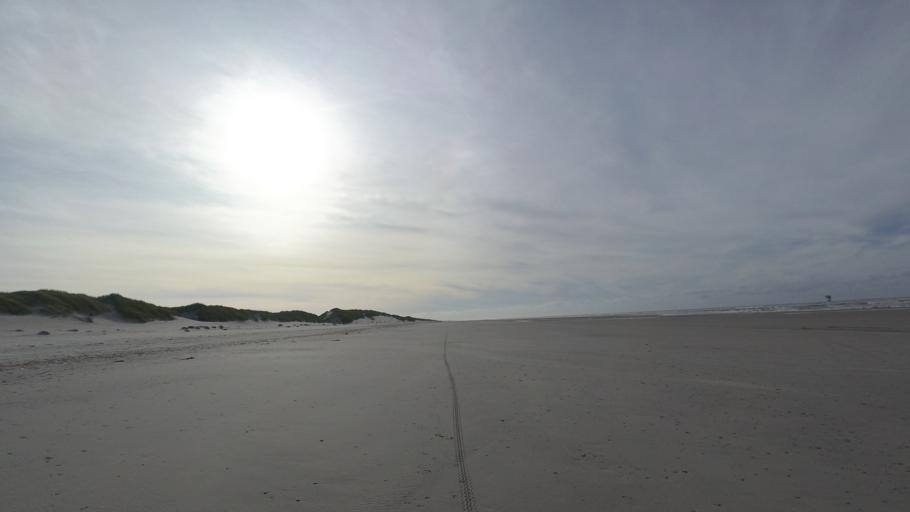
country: NL
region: Friesland
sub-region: Gemeente Dongeradeel
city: Holwerd
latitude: 53.4672
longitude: 5.9001
